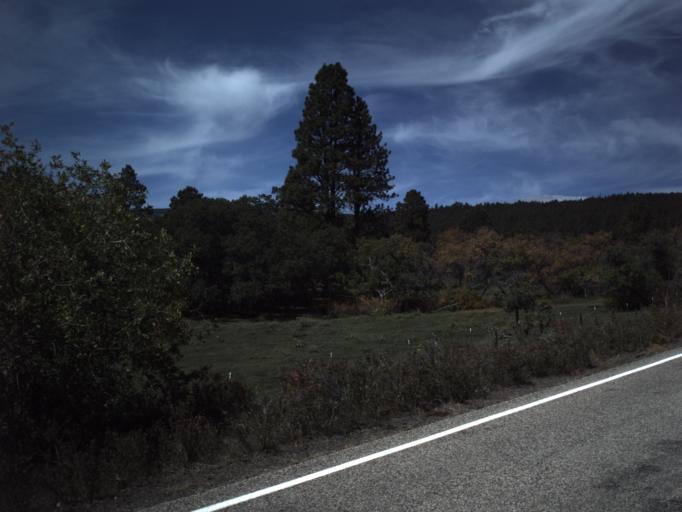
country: US
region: Utah
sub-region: Wayne County
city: Loa
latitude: 37.9926
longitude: -111.4299
